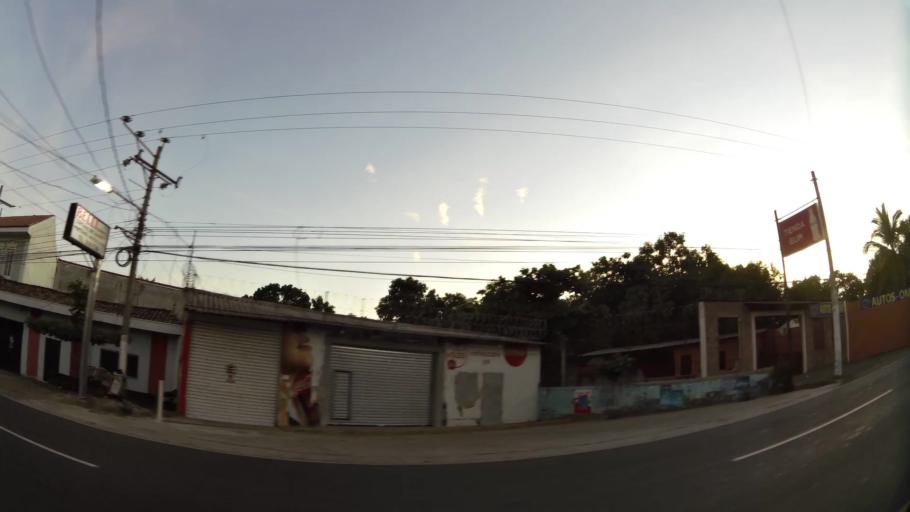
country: SV
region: San Miguel
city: San Miguel
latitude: 13.4966
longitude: -88.2029
